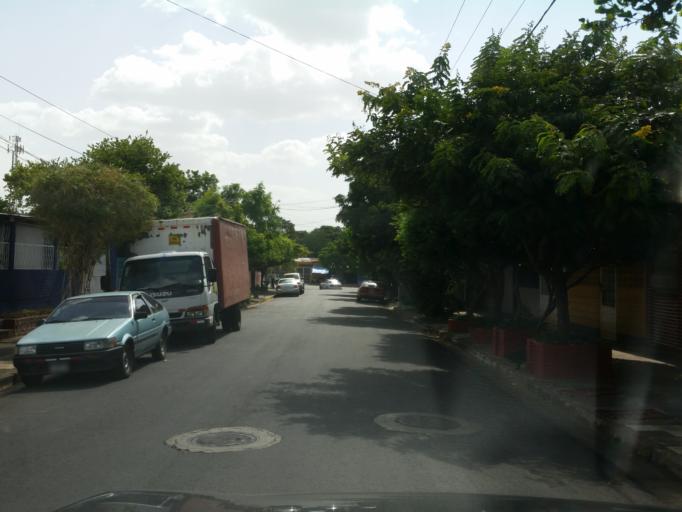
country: NI
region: Managua
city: Managua
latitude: 12.1288
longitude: -86.2553
